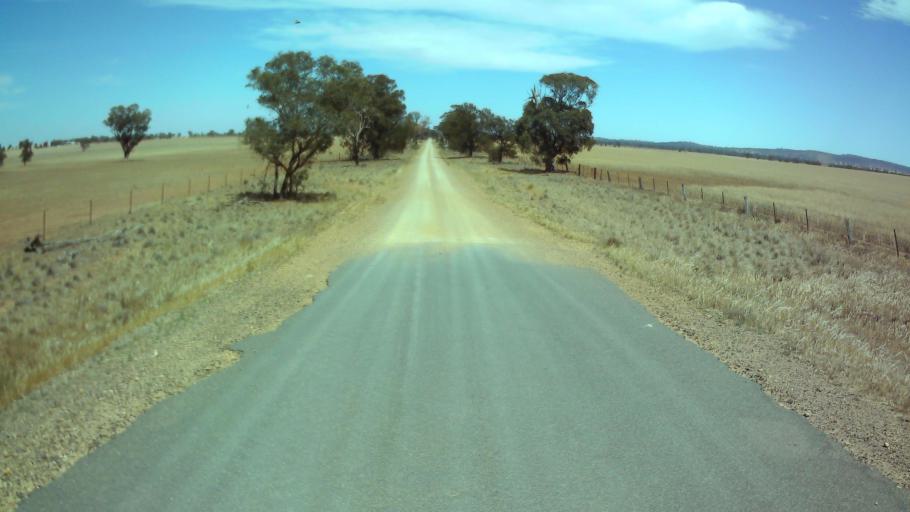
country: AU
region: New South Wales
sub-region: Weddin
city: Grenfell
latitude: -33.8593
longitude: 147.9285
